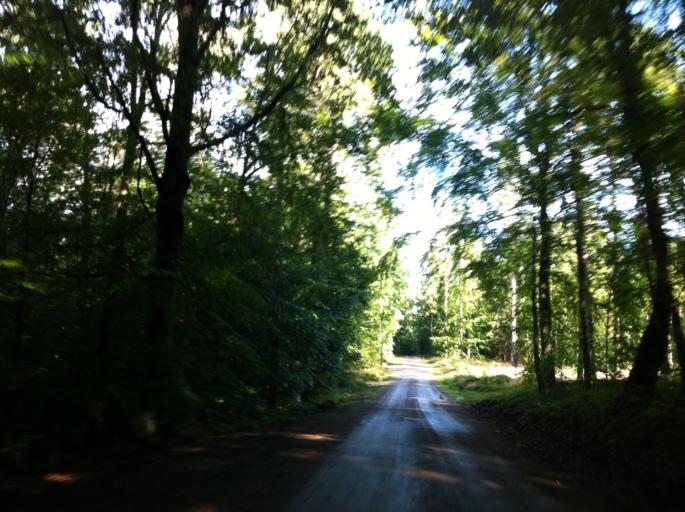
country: SE
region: Skane
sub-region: Hassleholms Kommun
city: Sosdala
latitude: 56.1334
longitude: 13.5573
